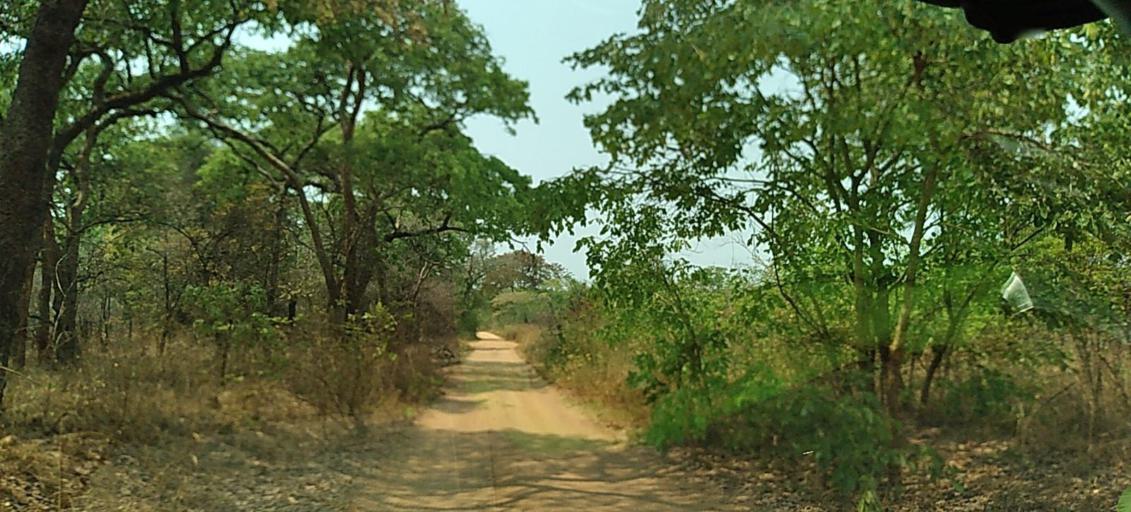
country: ZM
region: North-Western
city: Kabompo
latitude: -13.7074
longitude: 24.3242
